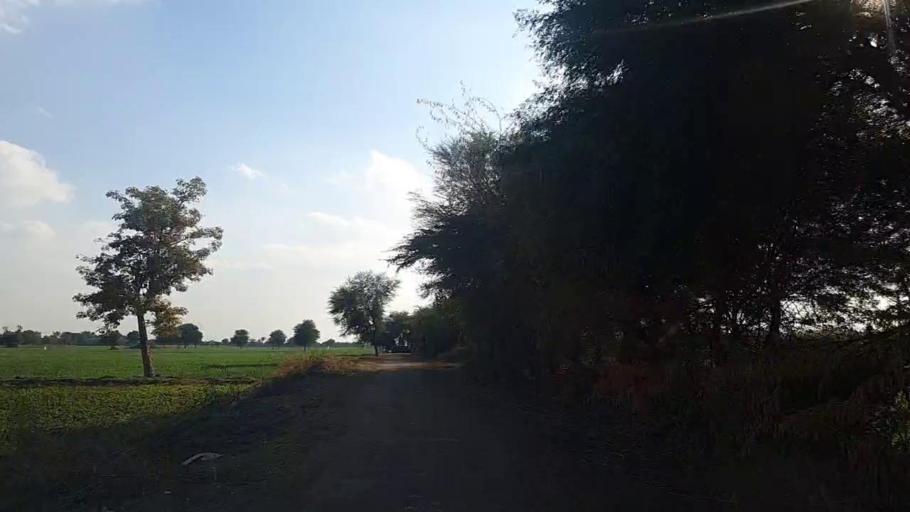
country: PK
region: Sindh
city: Tando Mittha Khan
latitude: 25.9421
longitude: 69.2116
